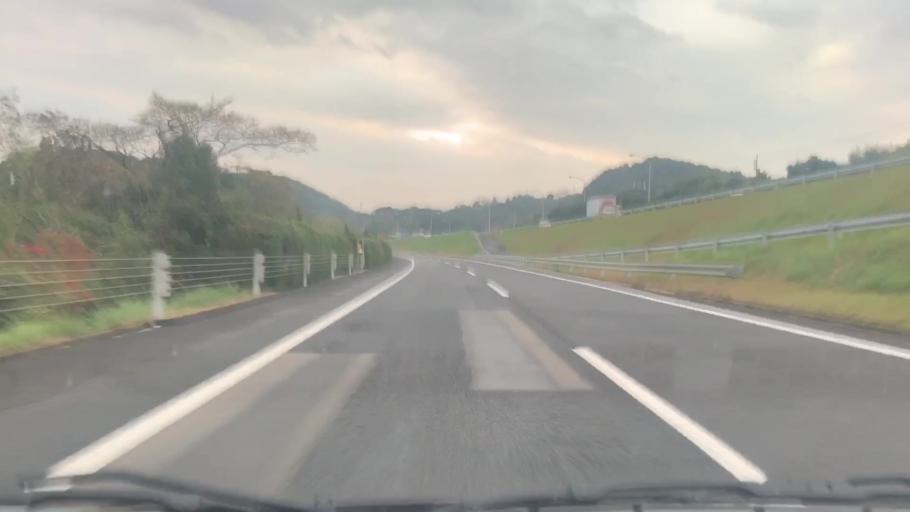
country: JP
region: Nagasaki
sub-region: Isahaya-shi
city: Isahaya
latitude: 32.8643
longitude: 130.0005
